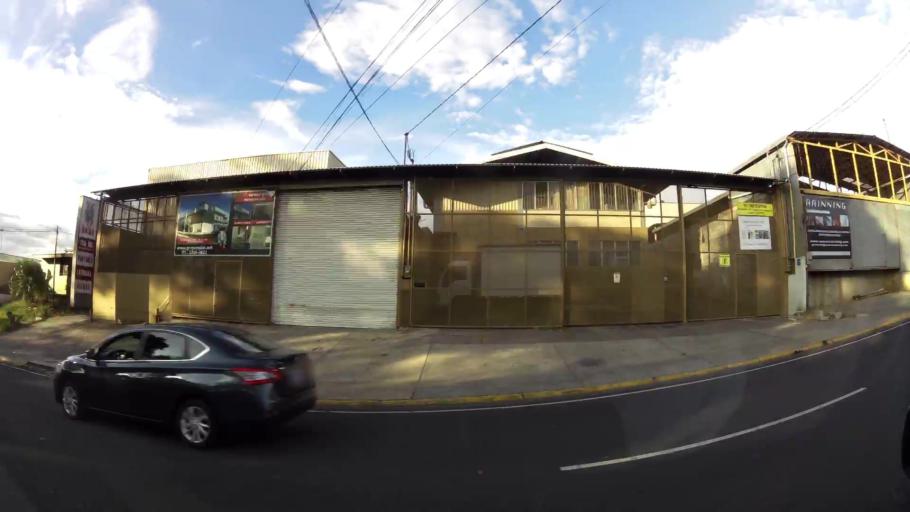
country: CR
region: Heredia
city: Llorente
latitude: 10.0027
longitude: -84.1647
